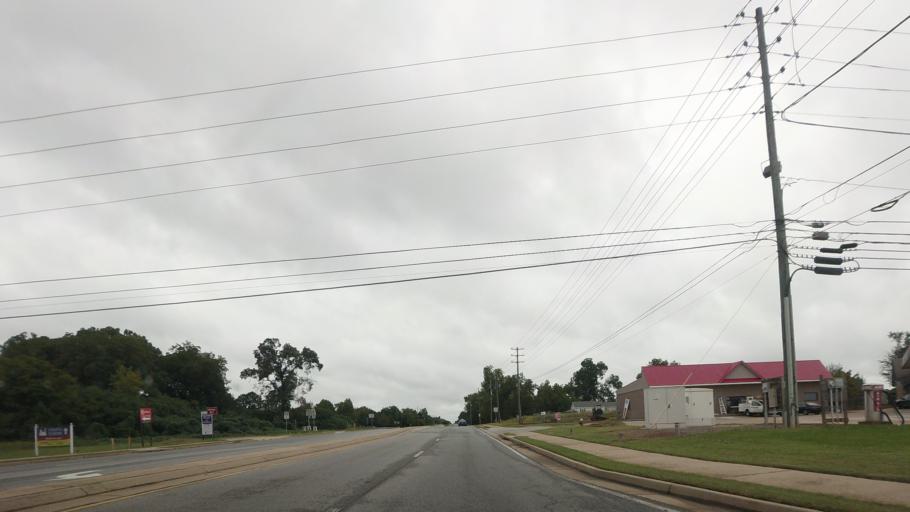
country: US
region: Georgia
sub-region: Houston County
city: Perry
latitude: 32.5061
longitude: -83.6625
